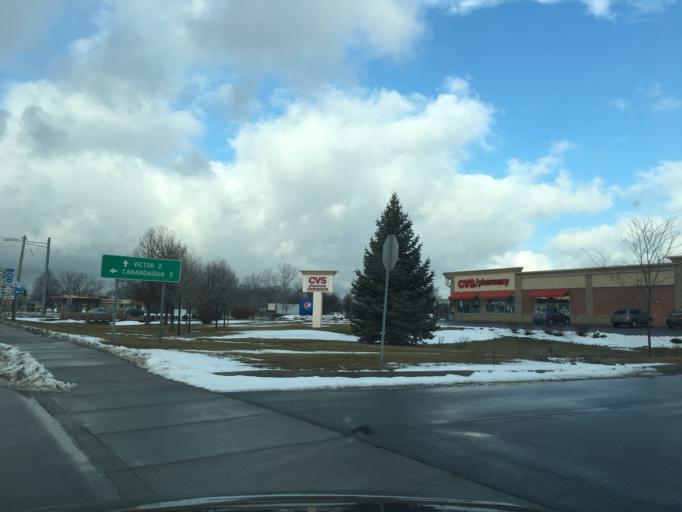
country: US
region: New York
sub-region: Ontario County
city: Victor
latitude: 42.9745
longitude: -77.3544
